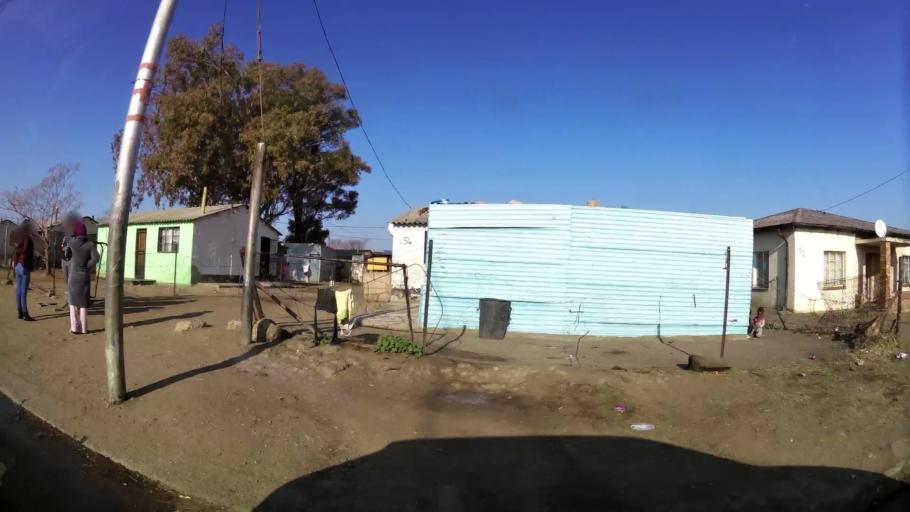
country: ZA
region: Orange Free State
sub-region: Mangaung Metropolitan Municipality
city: Bloemfontein
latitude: -29.1364
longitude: 26.2441
